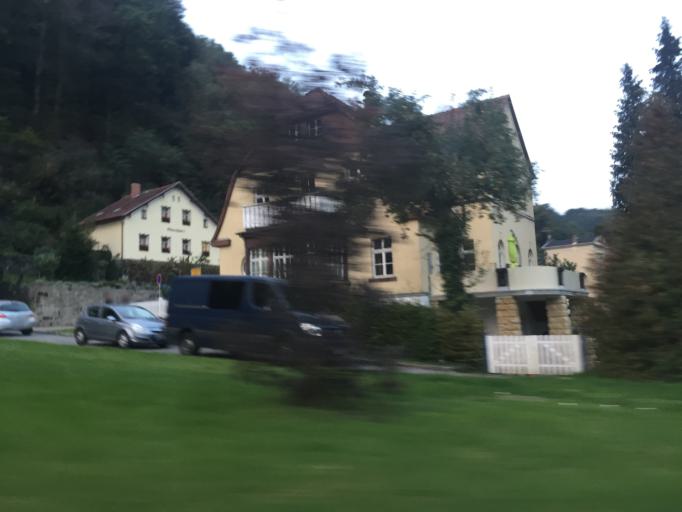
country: DE
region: Saxony
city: Rathmannsdorf
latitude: 50.9206
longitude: 14.1451
